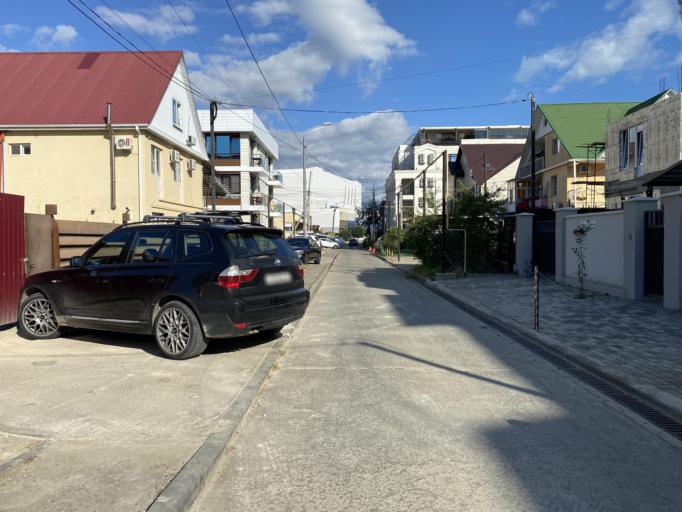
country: RU
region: Krasnodarskiy
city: Adler
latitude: 43.4104
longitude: 39.9590
